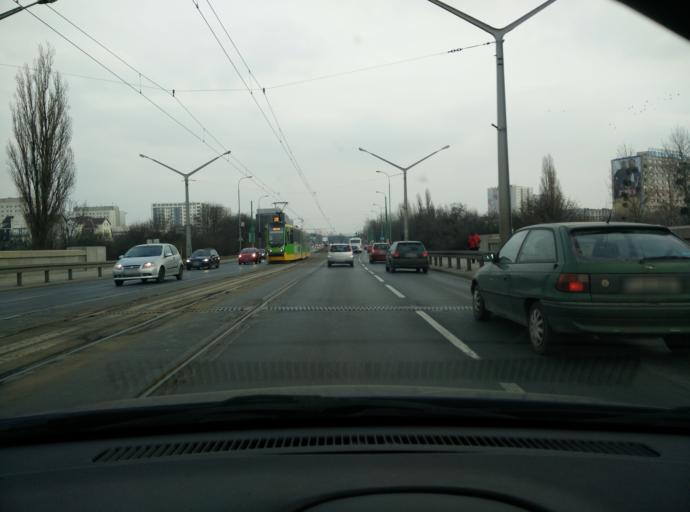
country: PL
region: Greater Poland Voivodeship
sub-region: Poznan
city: Poznan
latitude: 52.3978
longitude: 16.9416
